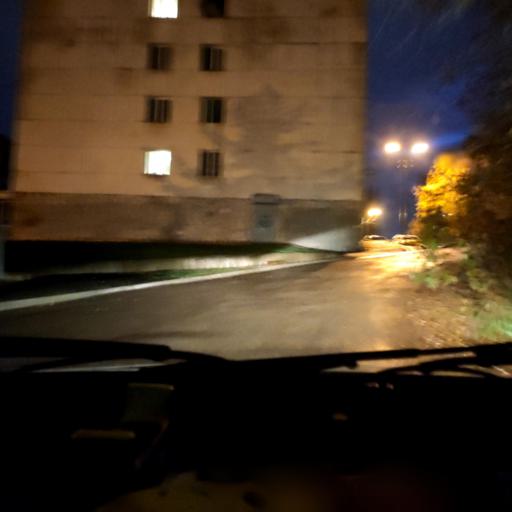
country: RU
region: Bashkortostan
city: Ufa
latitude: 54.7462
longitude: 55.9608
